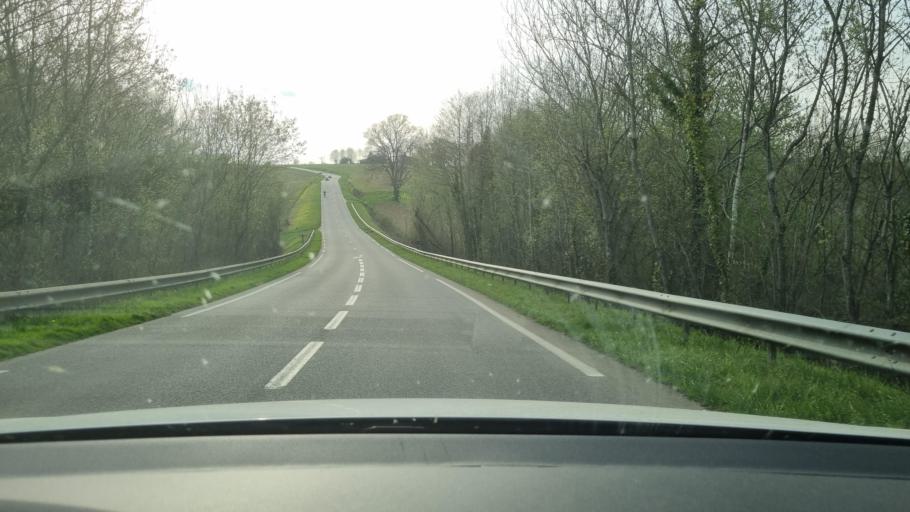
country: FR
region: Aquitaine
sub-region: Departement des Pyrenees-Atlantiques
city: Morlaas
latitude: 43.3709
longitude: -0.1794
